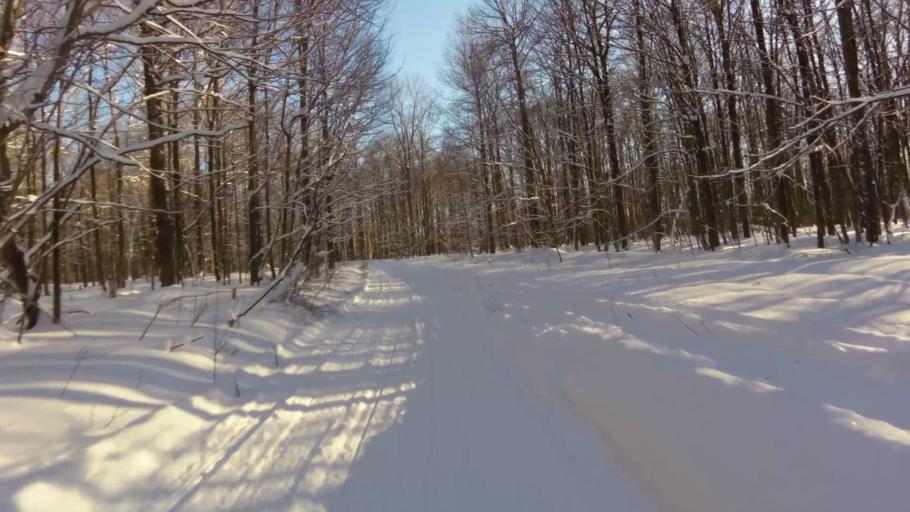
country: US
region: New York
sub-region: Chautauqua County
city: Falconer
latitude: 42.2300
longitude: -79.2194
